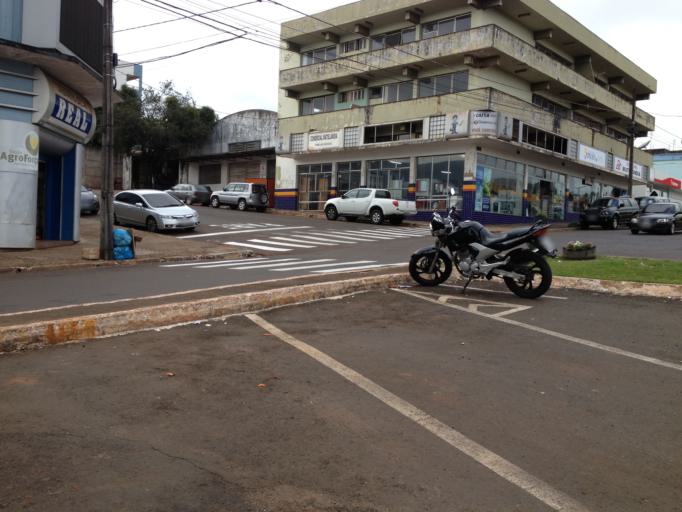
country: BR
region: Parana
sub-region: Matelandia
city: Matelandia
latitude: -25.2423
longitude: -53.9796
